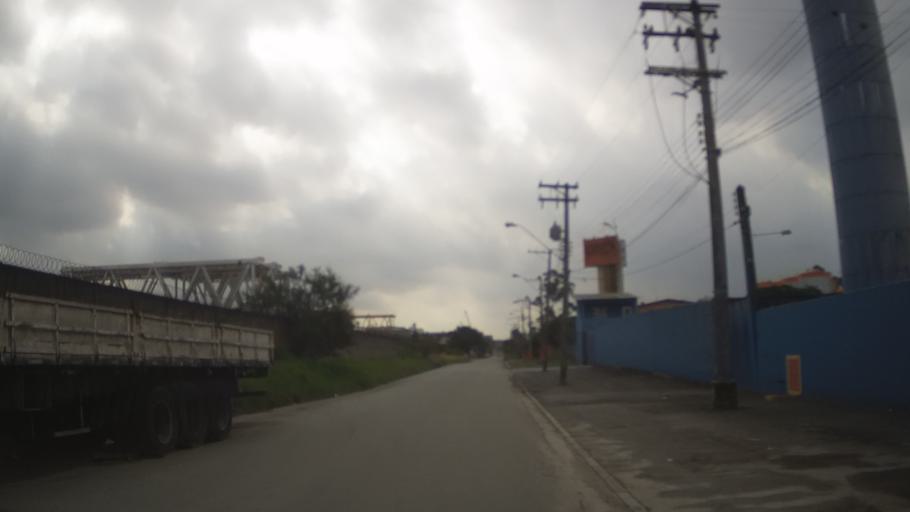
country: BR
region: Sao Paulo
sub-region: Guarulhos
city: Guarulhos
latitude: -23.4726
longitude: -46.4811
